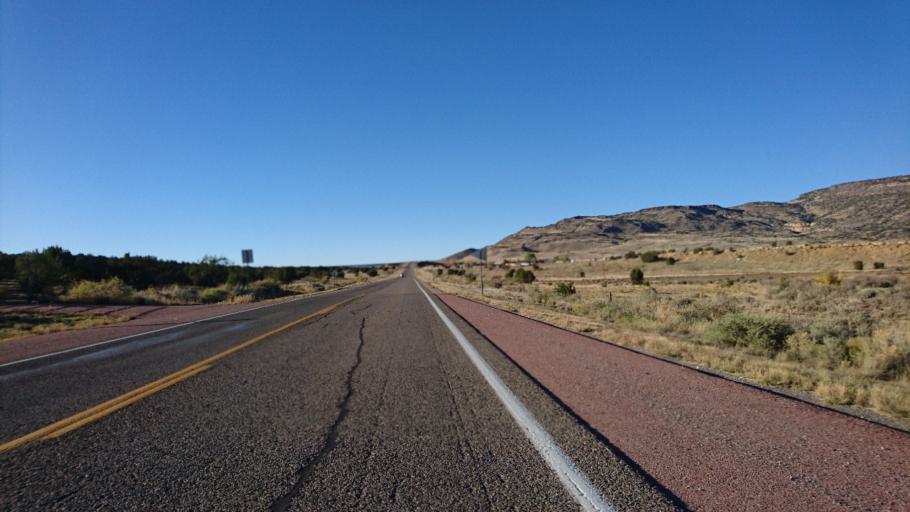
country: US
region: New Mexico
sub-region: Cibola County
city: Grants
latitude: 35.0981
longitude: -107.7740
